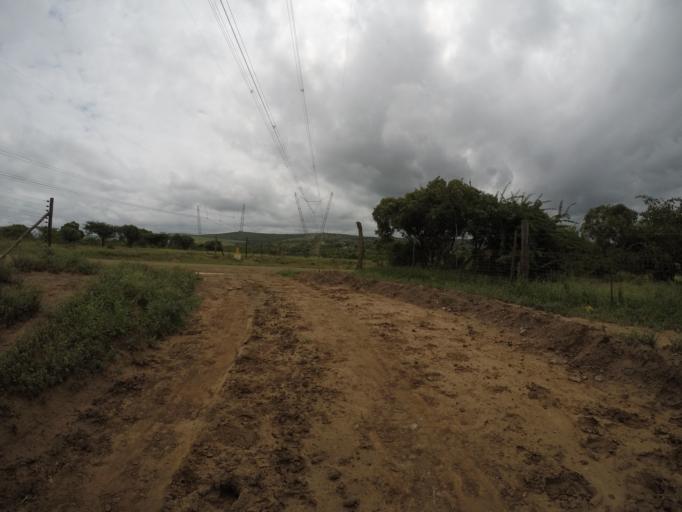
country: ZA
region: KwaZulu-Natal
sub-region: uThungulu District Municipality
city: Empangeni
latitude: -28.6034
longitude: 31.8267
